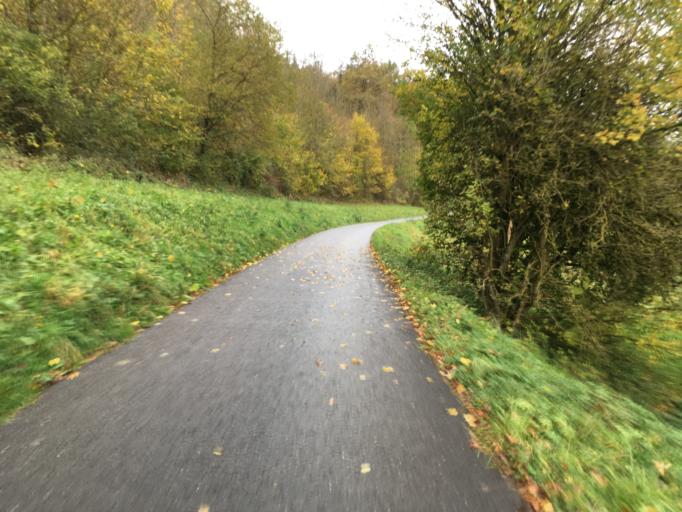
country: DE
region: Baden-Wuerttemberg
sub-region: Regierungsbezirk Stuttgart
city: Widdern
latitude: 49.3325
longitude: 9.4215
